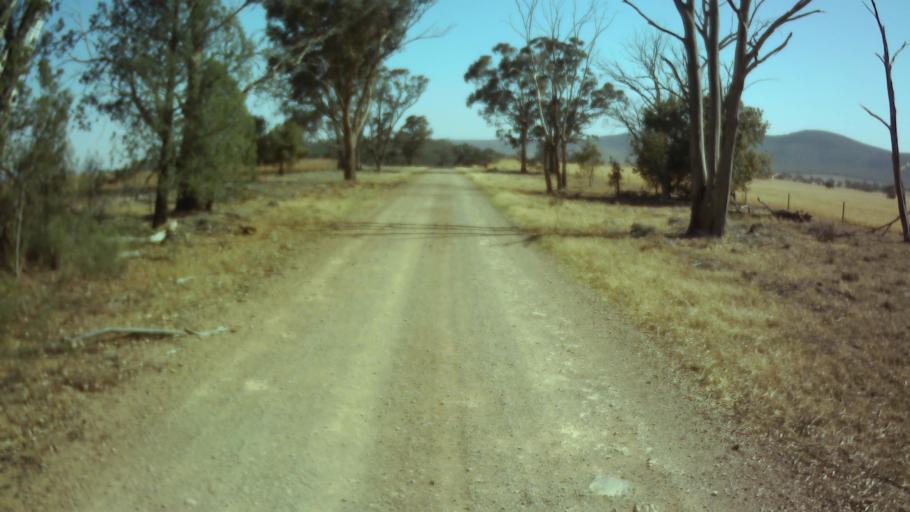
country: AU
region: New South Wales
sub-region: Weddin
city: Grenfell
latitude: -33.8511
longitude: 148.0164
